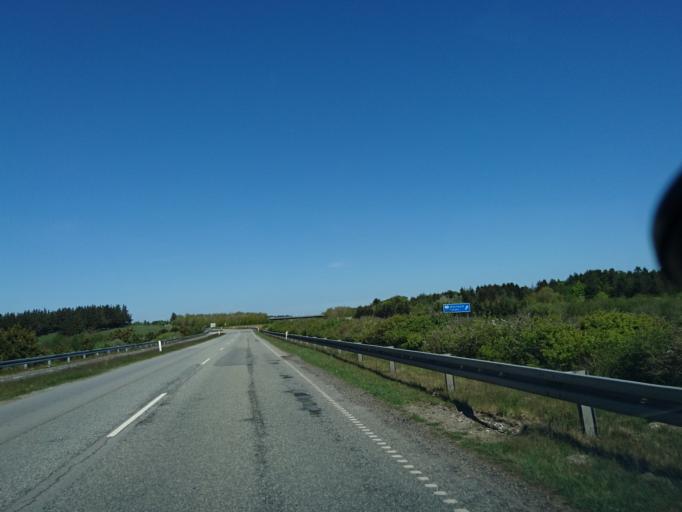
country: DK
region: North Denmark
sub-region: Hjorring Kommune
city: Hjorring
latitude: 57.5064
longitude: 10.0055
